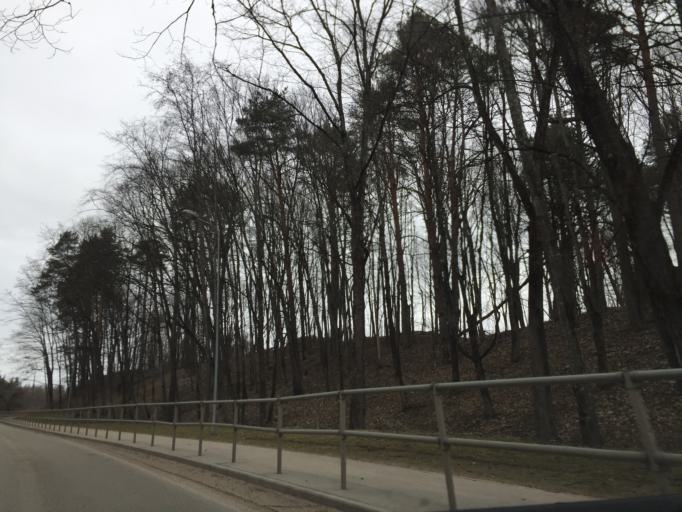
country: LV
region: Kraslavas Rajons
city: Kraslava
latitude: 55.9014
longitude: 27.1564
